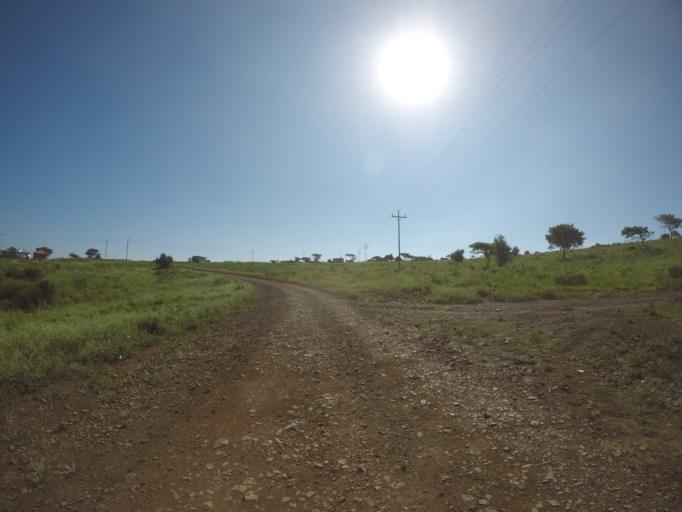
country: ZA
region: KwaZulu-Natal
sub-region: uThungulu District Municipality
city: Empangeni
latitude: -28.5714
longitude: 31.7193
